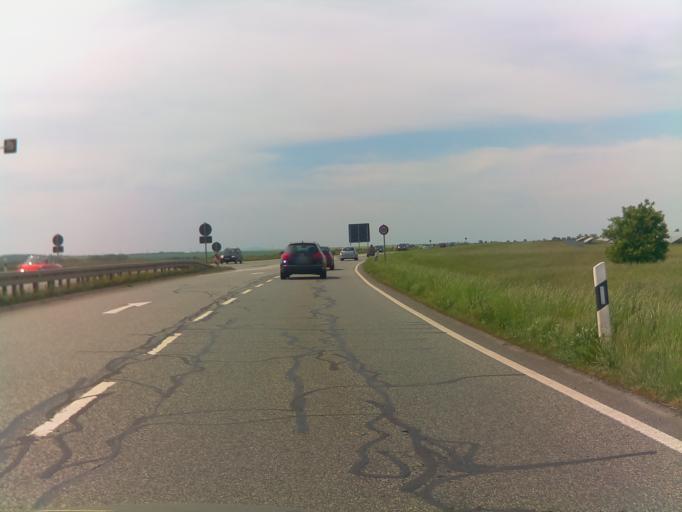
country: DE
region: Saxony-Anhalt
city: Westeregeln
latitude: 51.9410
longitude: 11.4061
